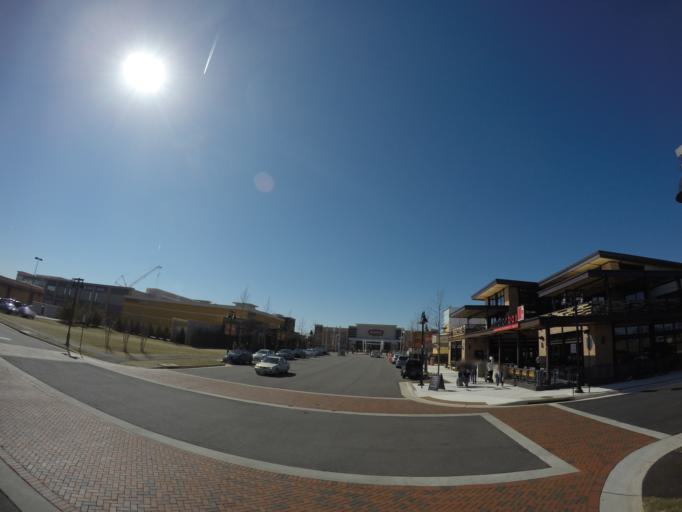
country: US
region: Virginia
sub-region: Loudoun County
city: University Center
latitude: 39.0523
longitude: -77.4529
